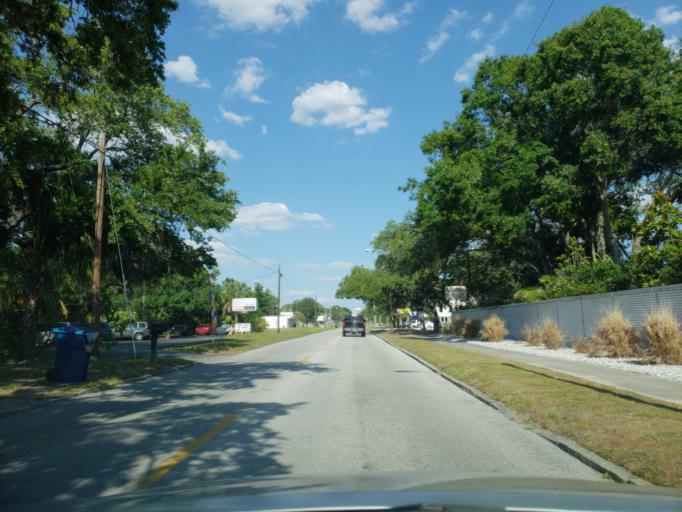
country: US
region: Florida
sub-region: Hillsborough County
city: Tampa
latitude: 27.9521
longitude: -82.4989
